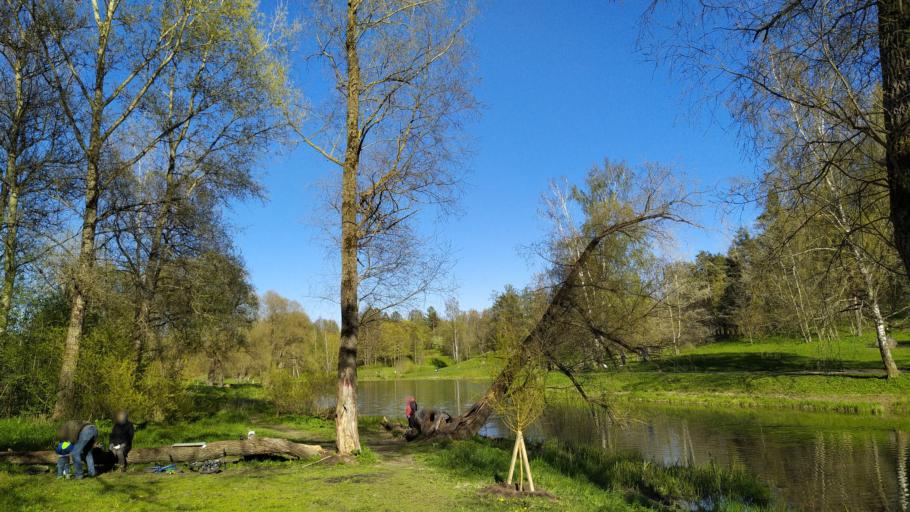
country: RU
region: St.-Petersburg
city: Pavlovsk
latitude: 59.6827
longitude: 30.4456
